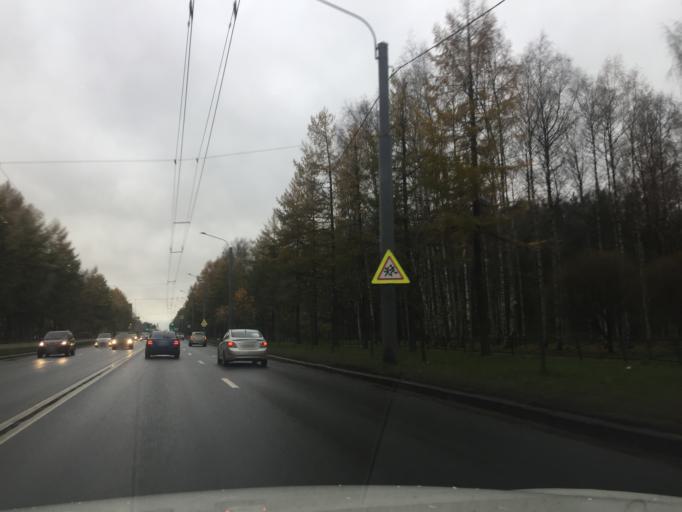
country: RU
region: St.-Petersburg
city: Sosnovka
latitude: 60.0173
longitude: 30.3636
